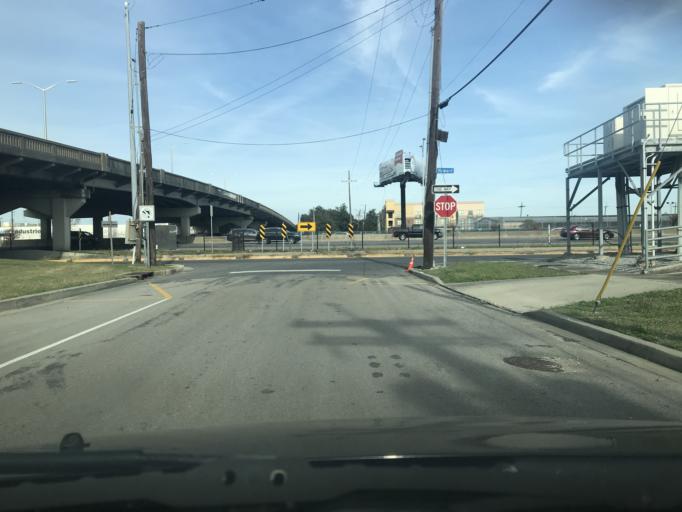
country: US
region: Louisiana
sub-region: Orleans Parish
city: New Orleans
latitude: 29.9618
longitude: -90.1010
